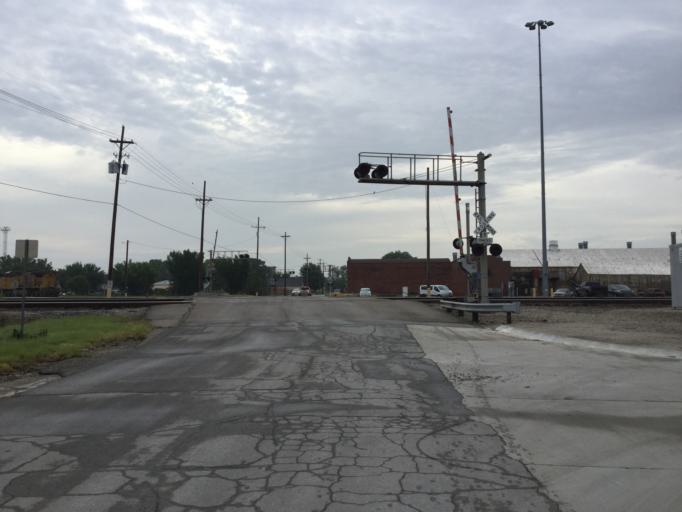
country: US
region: Kansas
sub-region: Montgomery County
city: Coffeyville
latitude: 37.0287
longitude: -95.6249
